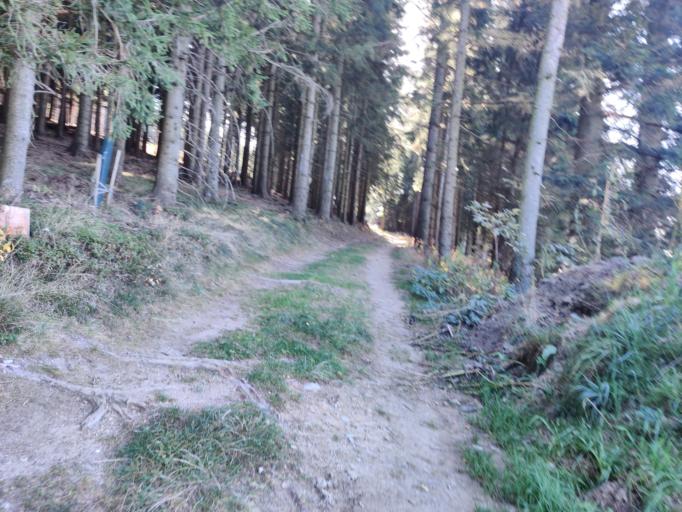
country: AT
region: Styria
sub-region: Politischer Bezirk Hartberg-Fuerstenfeld
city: Sankt Jakob im Walde
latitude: 47.4762
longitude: 15.8008
